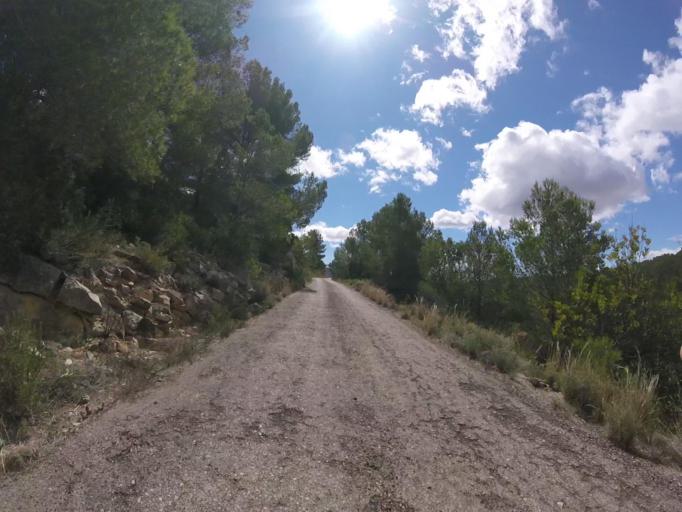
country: ES
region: Valencia
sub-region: Provincia de Castello
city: Adzaneta
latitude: 40.2696
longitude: -0.1056
